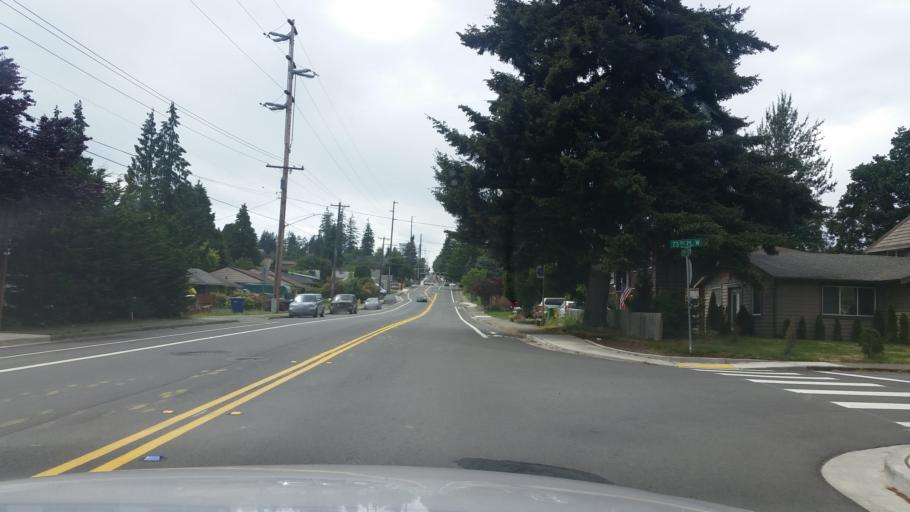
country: US
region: Washington
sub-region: Snohomish County
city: Mountlake Terrace
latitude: 47.7924
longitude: -122.3317
